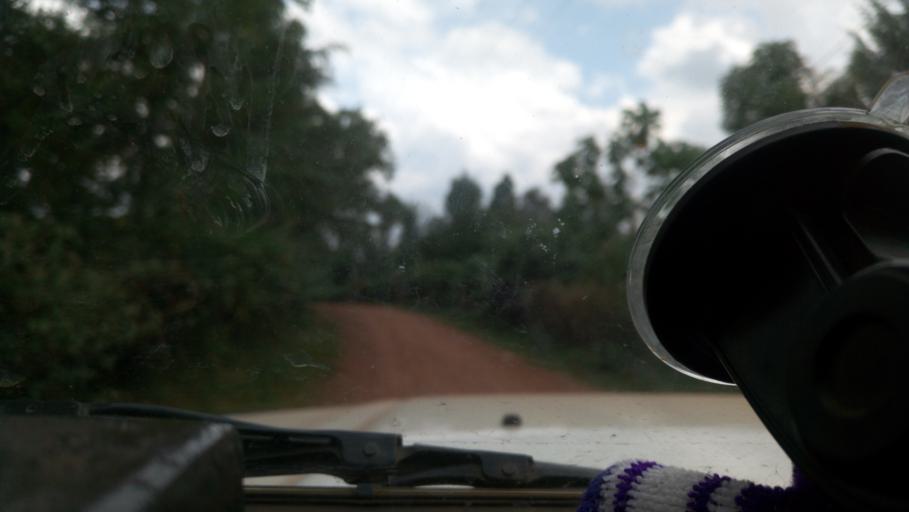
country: KE
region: Kericho
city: Litein
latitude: -0.6085
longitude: 35.1760
